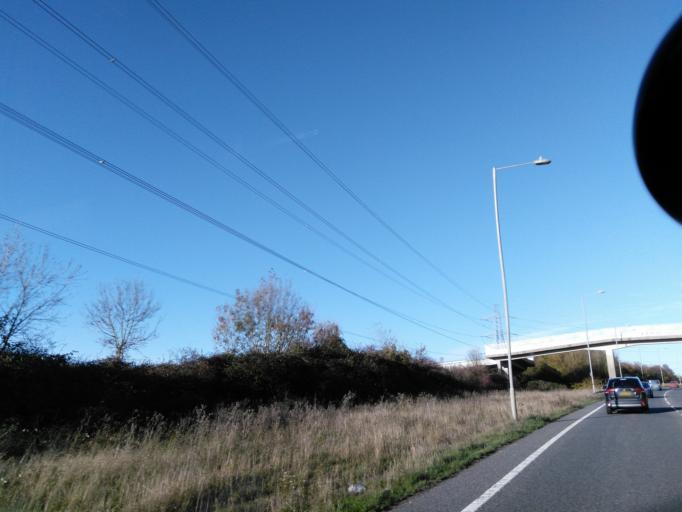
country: GB
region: England
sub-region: Wiltshire
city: Chippenham
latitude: 51.4620
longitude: -2.1503
